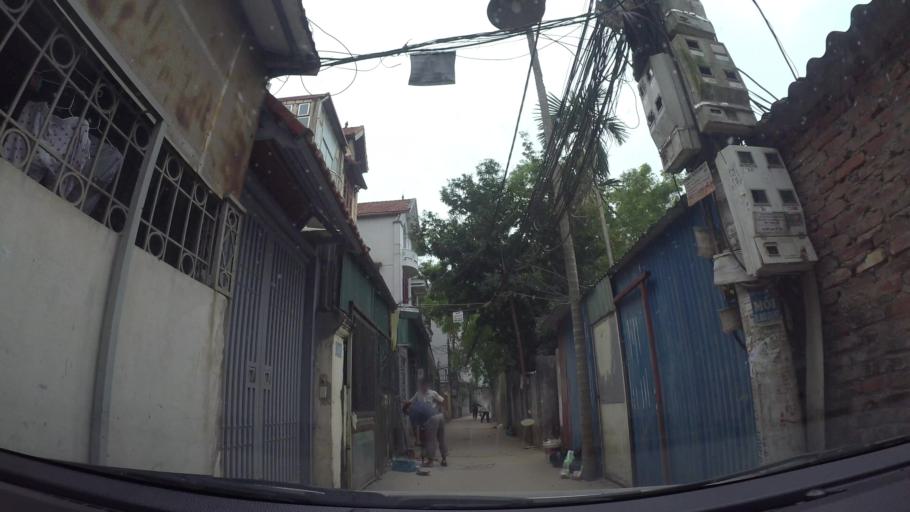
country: VN
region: Ha Noi
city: Tay Ho
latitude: 21.0836
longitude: 105.8188
